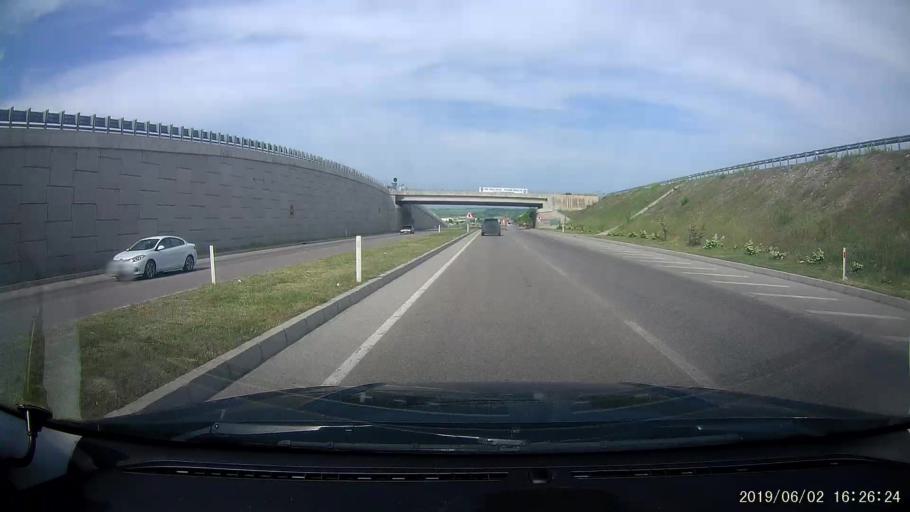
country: TR
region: Samsun
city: Ladik
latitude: 40.9995
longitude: 35.8013
